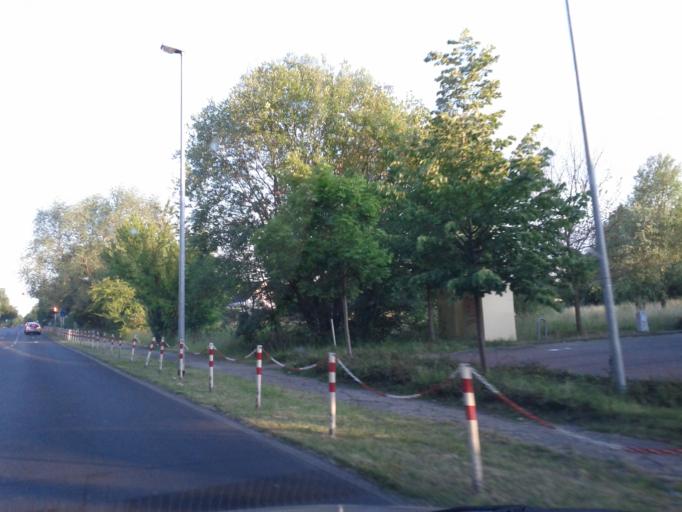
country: DE
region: Berlin
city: Hellersdorf
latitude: 52.5403
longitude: 13.6389
